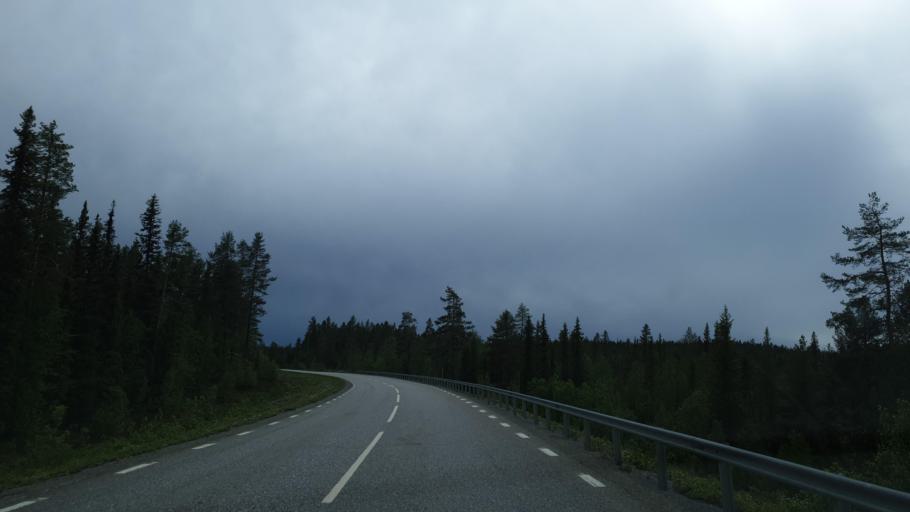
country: SE
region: Vaesterbotten
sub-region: Storumans Kommun
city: Fristad
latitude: 65.4818
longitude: 16.8957
